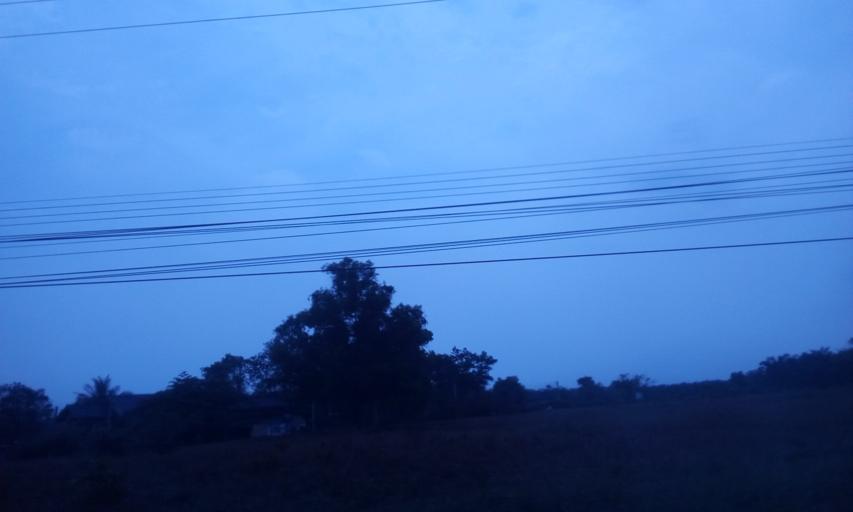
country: TH
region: Trat
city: Khao Saming
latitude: 12.3946
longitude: 102.3590
